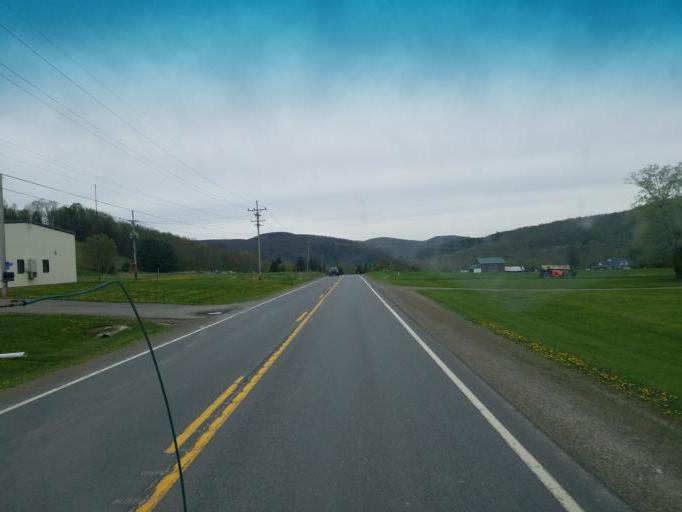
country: US
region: Pennsylvania
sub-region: Tioga County
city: Westfield
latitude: 41.8996
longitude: -77.5332
